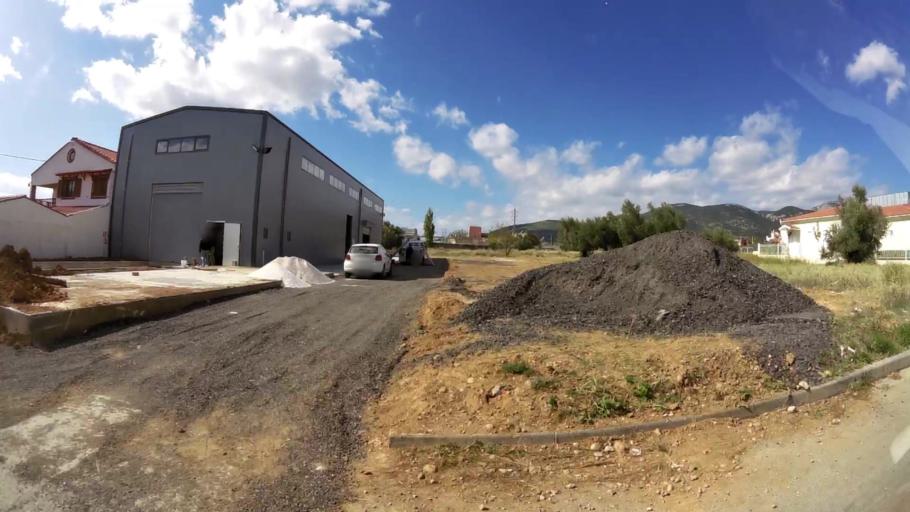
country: GR
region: Attica
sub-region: Nomarchia Anatolikis Attikis
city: Acharnes
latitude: 38.0999
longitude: 23.7472
